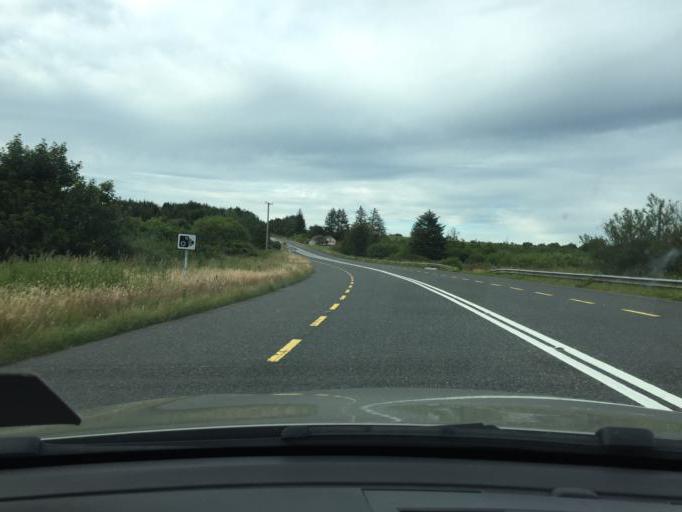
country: IE
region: Munster
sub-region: Waterford
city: Dungarvan
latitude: 52.0386
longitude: -7.6613
